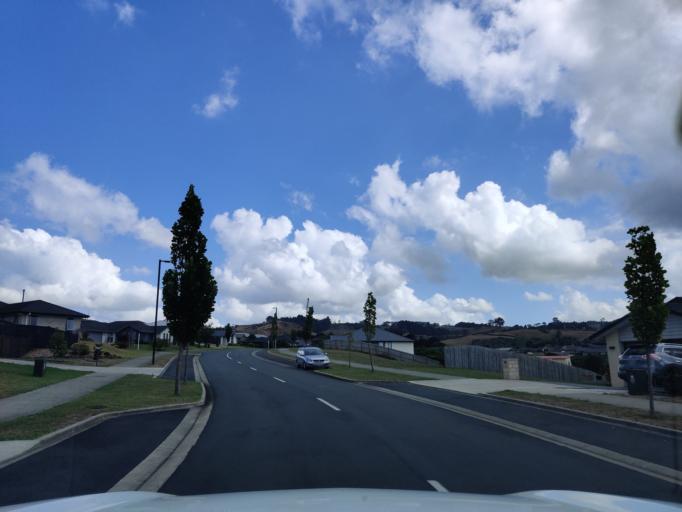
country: NZ
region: Auckland
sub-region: Auckland
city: Pukekohe East
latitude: -37.2370
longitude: 175.0118
